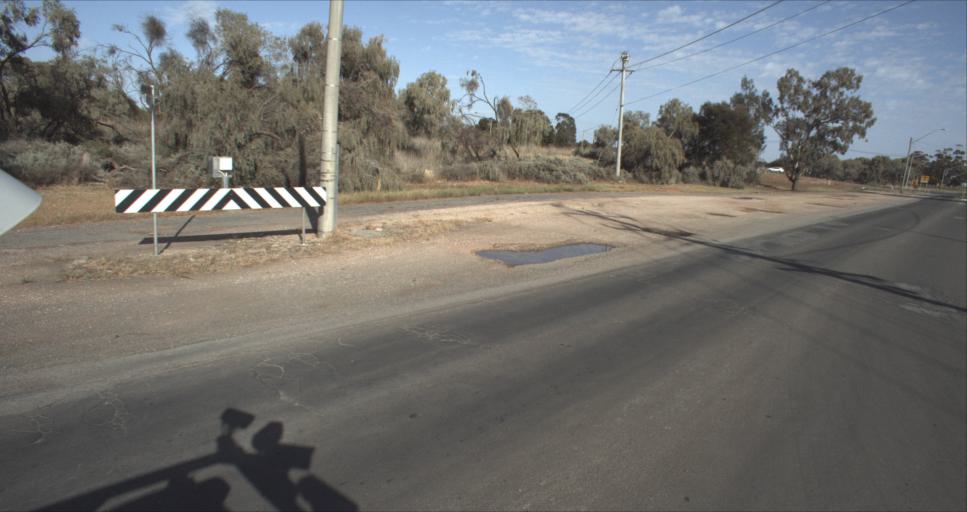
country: AU
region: New South Wales
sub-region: Leeton
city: Leeton
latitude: -34.5530
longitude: 146.3864
